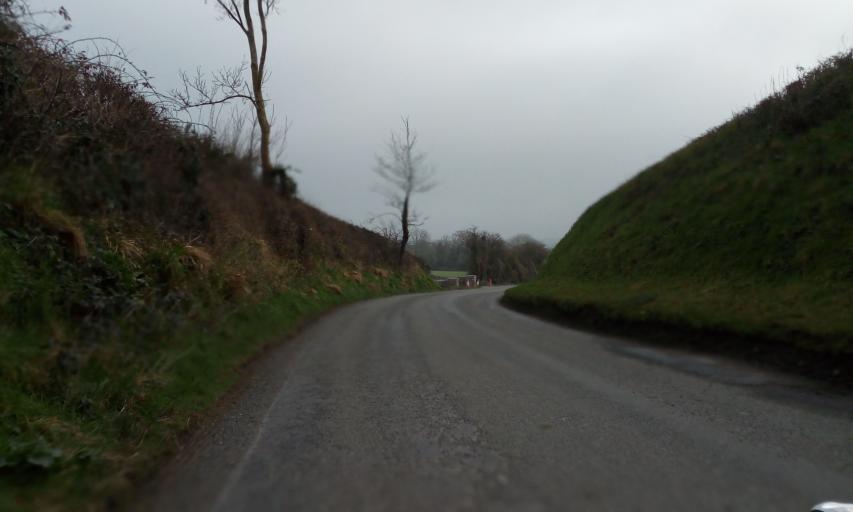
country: IE
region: Leinster
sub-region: Kilkenny
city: Kilkenny
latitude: 52.6583
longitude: -7.1775
